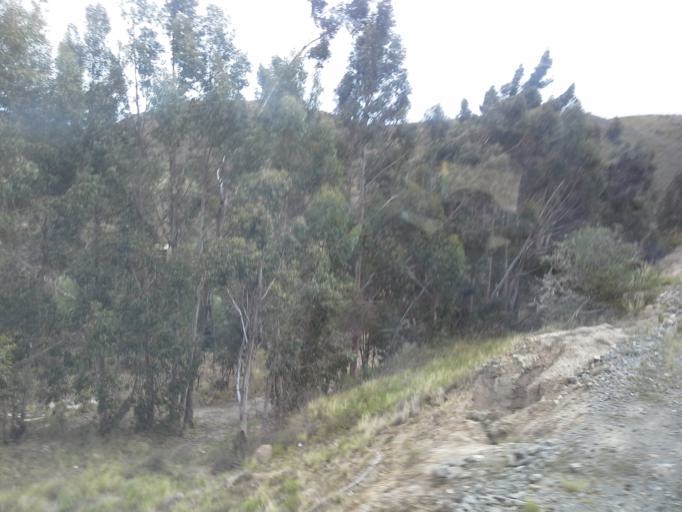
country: BO
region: Cochabamba
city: Colomi
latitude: -17.4023
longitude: -65.8143
